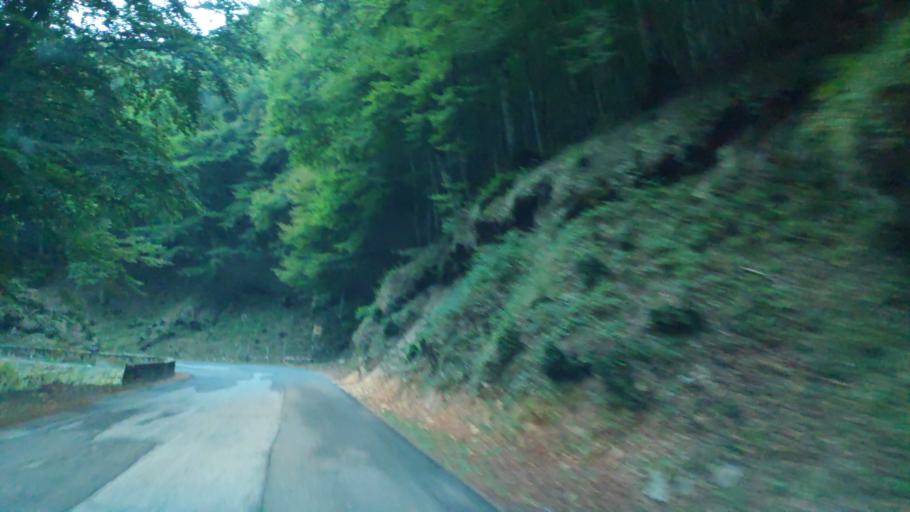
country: IT
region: Calabria
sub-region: Provincia di Vibo-Valentia
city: Mongiana
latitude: 38.5091
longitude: 16.3525
